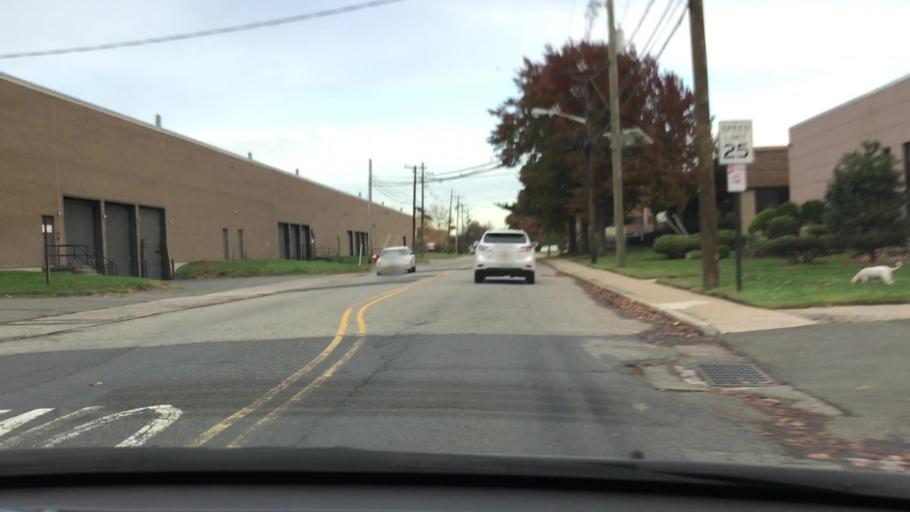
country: US
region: New Jersey
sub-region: Bergen County
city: Little Ferry
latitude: 40.8682
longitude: -74.0589
